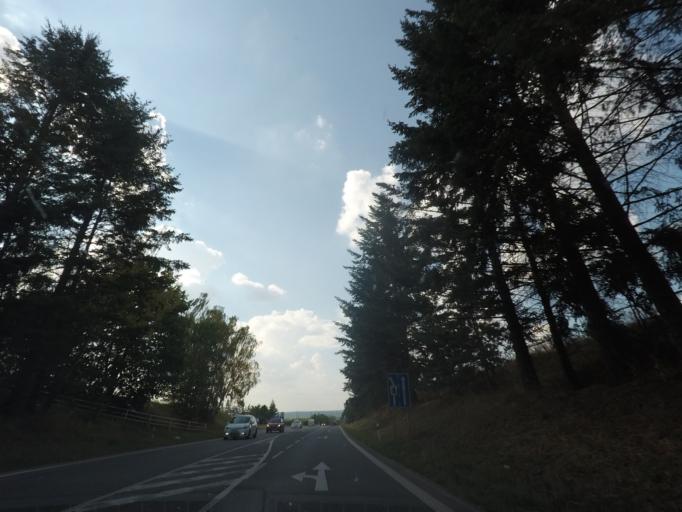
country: CZ
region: Kralovehradecky
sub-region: Okres Nachod
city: Jaromer
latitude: 50.4026
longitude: 15.8915
